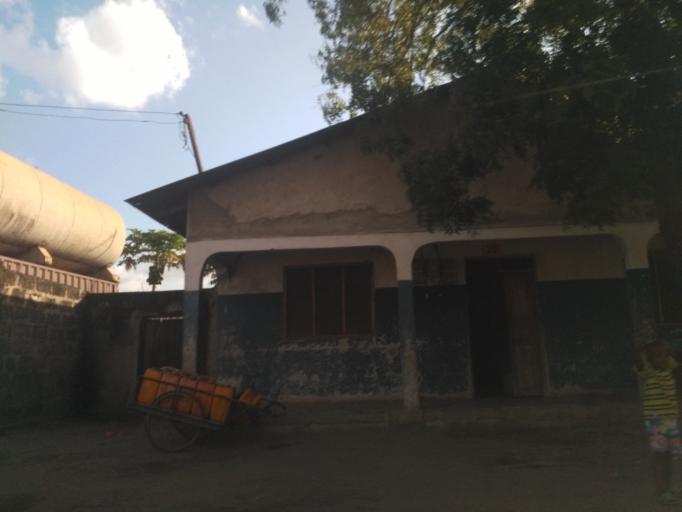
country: TZ
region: Dar es Salaam
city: Dar es Salaam
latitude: -6.8501
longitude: 39.2597
